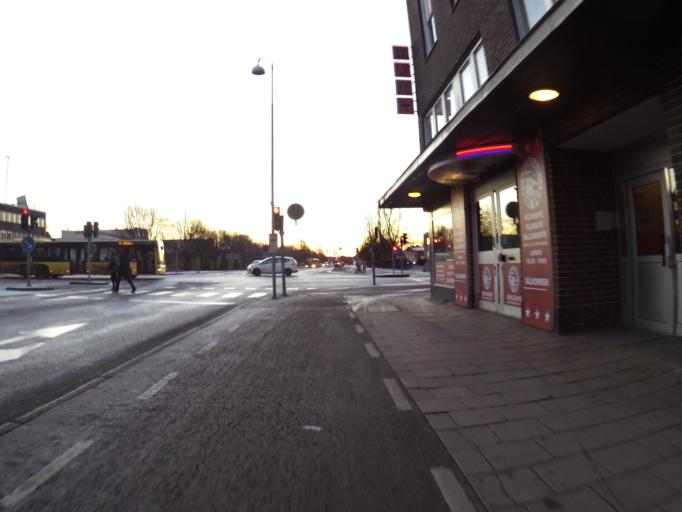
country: SE
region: Gaevleborg
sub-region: Gavle Kommun
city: Gavle
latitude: 60.6677
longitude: 17.1510
